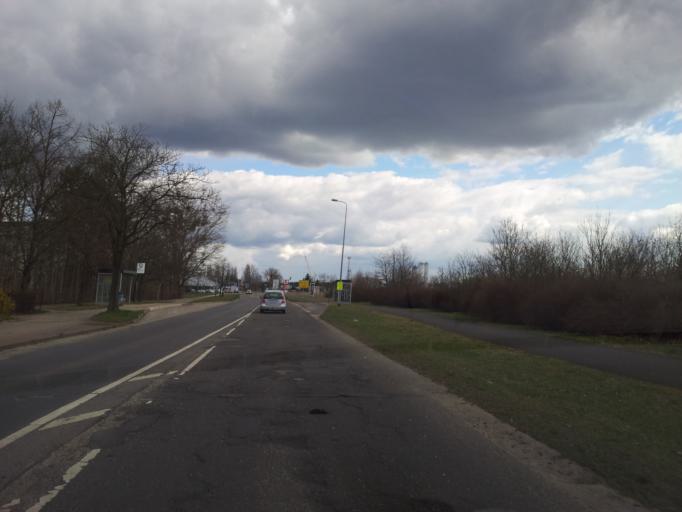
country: DE
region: Saxony
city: Hoyerswerda
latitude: 51.4293
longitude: 14.2728
